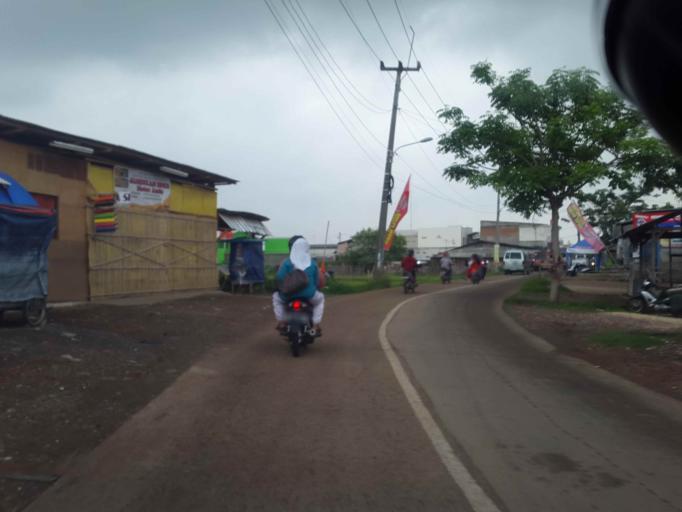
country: ID
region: West Java
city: Cikarang
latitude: -6.3270
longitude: 107.1829
